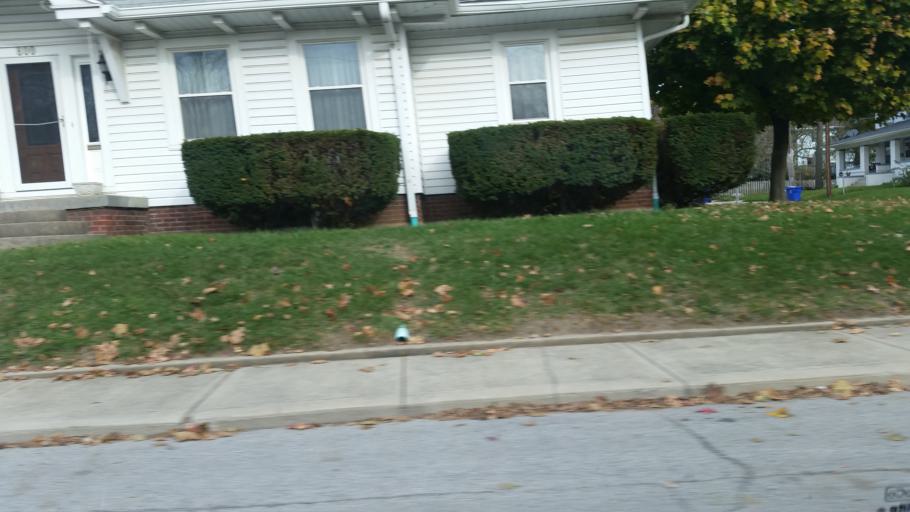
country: US
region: Indiana
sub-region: Howard County
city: Kokomo
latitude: 40.4854
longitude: -86.1397
